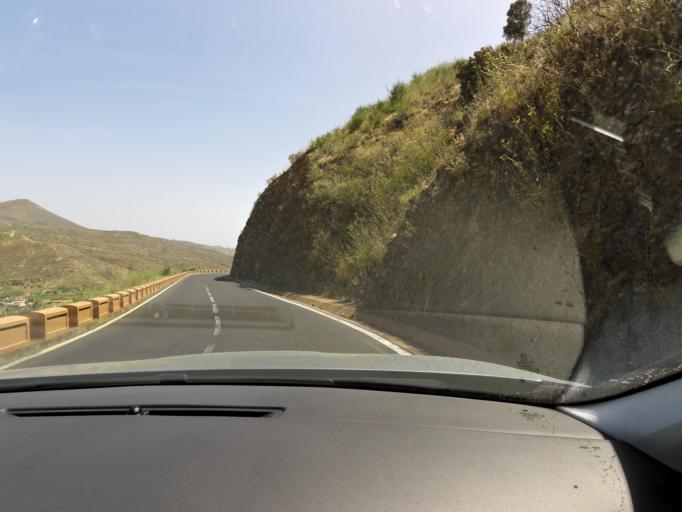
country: ES
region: Canary Islands
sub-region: Provincia de Santa Cruz de Tenerife
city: Santiago del Teide
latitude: 28.3125
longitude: -16.8071
